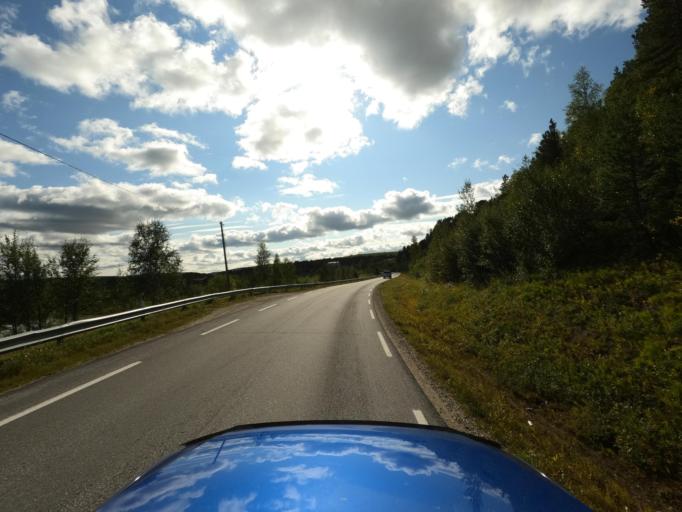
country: NO
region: Finnmark Fylke
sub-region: Karasjok
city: Karasjohka
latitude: 69.4053
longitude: 25.8085
